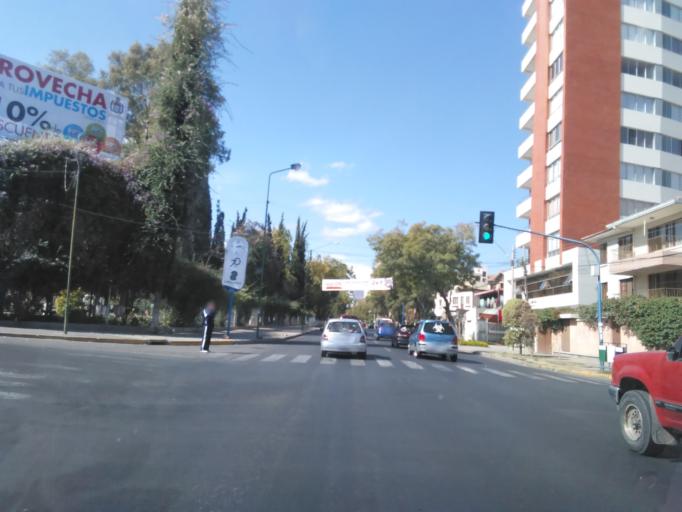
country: BO
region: Cochabamba
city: Cochabamba
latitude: -17.3817
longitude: -66.1569
